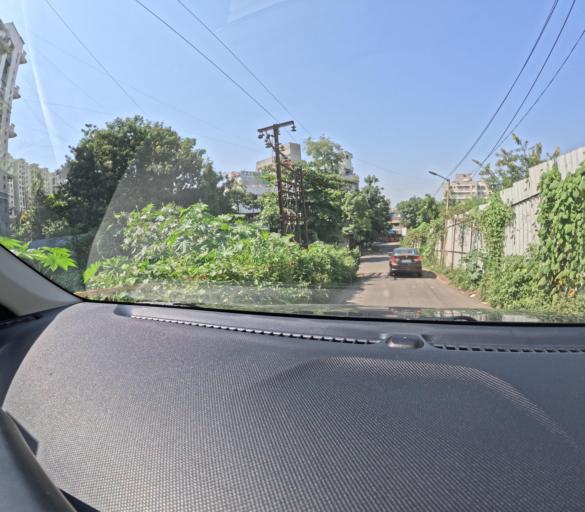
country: IN
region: Maharashtra
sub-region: Pune Division
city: Kharakvasla
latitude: 18.5093
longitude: 73.7820
